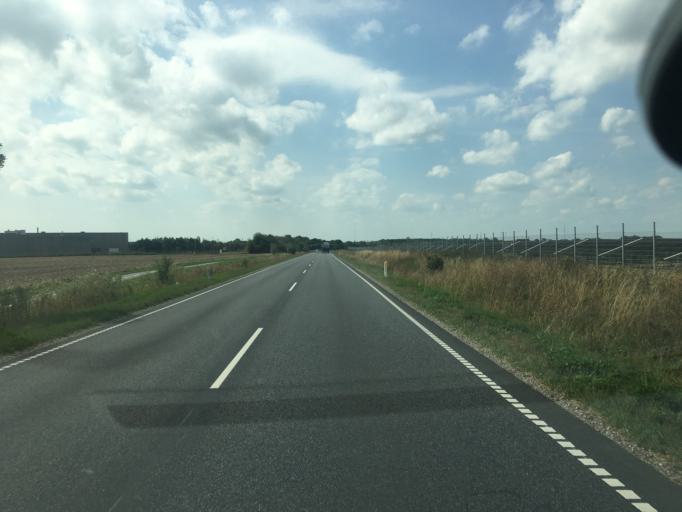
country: DK
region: South Denmark
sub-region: Aabenraa Kommune
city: Tinglev
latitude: 54.9481
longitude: 9.2743
